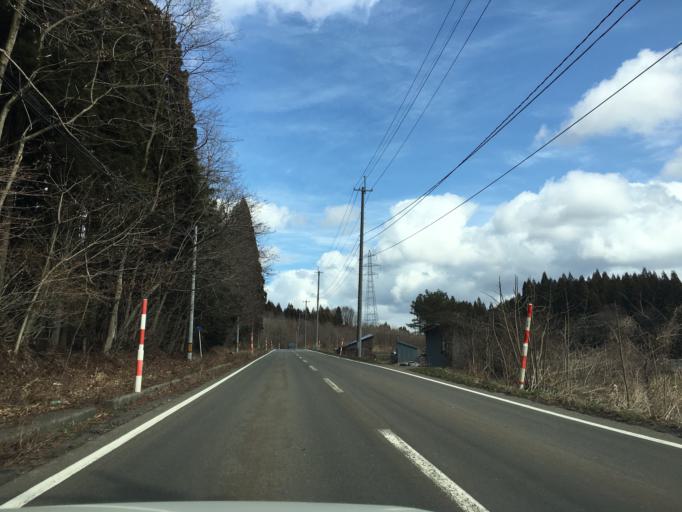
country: JP
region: Akita
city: Odate
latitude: 40.2013
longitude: 140.5402
